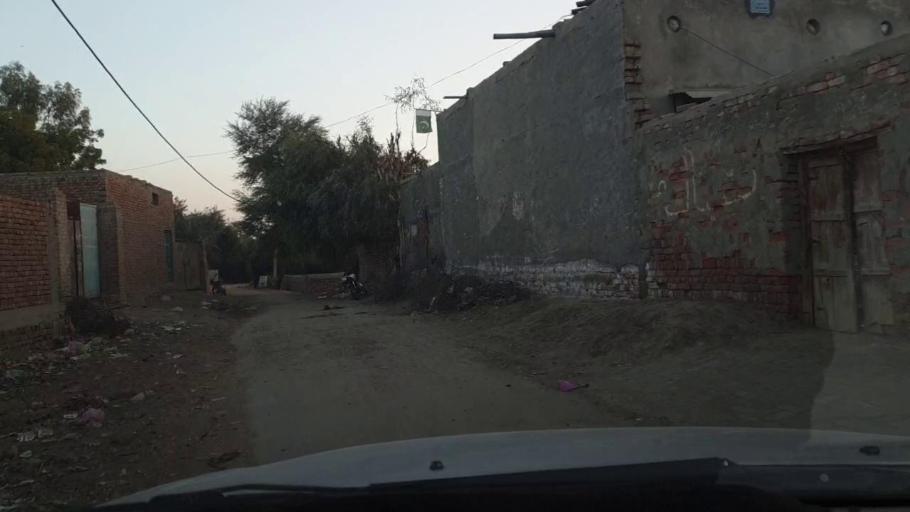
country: PK
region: Sindh
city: Mirpur Mathelo
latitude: 28.0203
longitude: 69.5661
